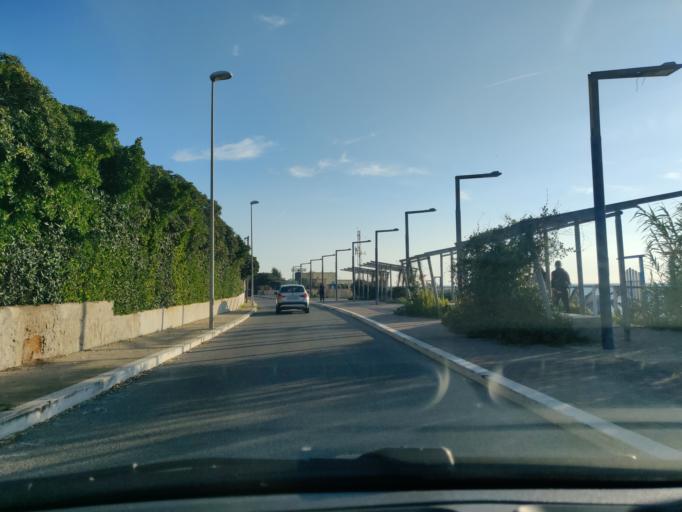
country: IT
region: Latium
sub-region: Citta metropolitana di Roma Capitale
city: Santa Marinella
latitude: 42.0354
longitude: 11.8333
